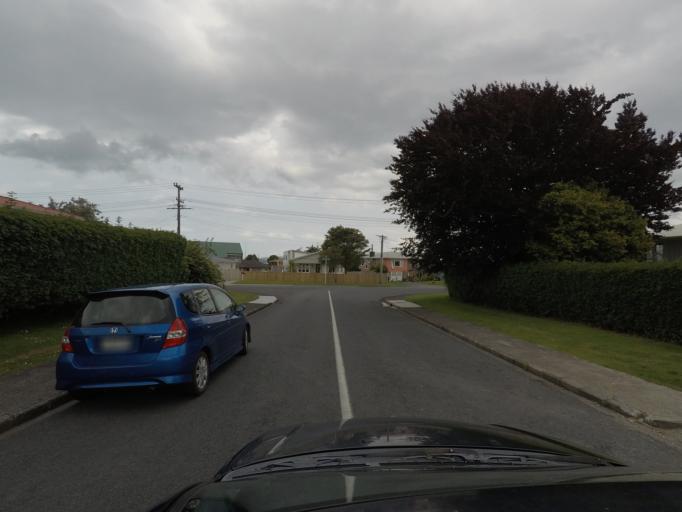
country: NZ
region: Auckland
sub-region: Auckland
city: Rosebank
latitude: -36.8478
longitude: 174.6494
